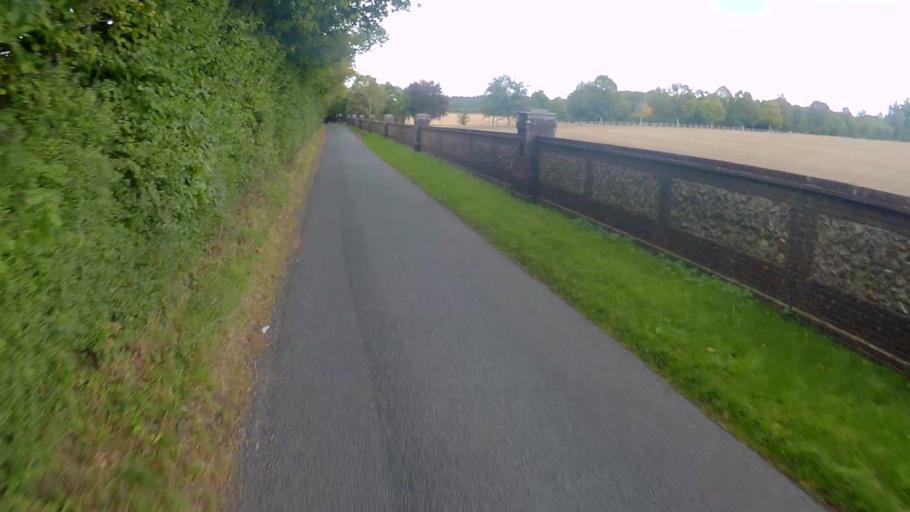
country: GB
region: England
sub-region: Hampshire
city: Overton
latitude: 51.1987
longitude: -1.2826
